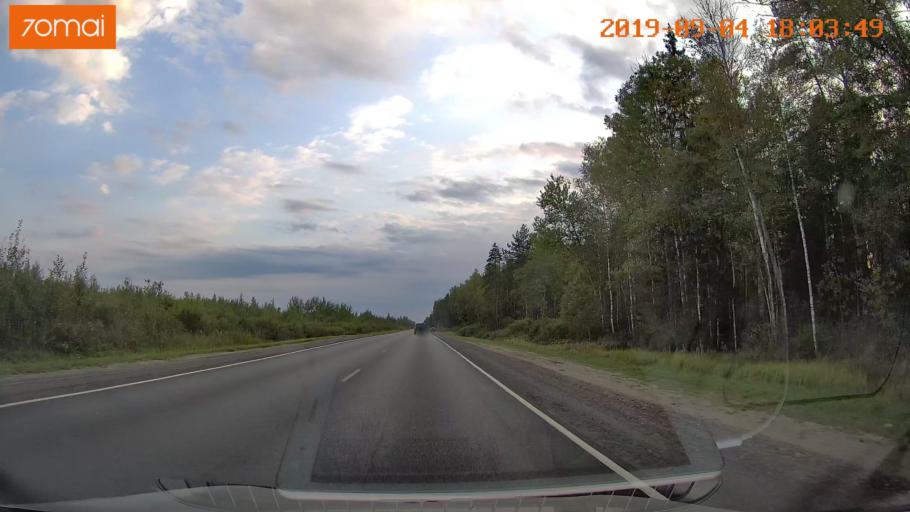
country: RU
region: Moskovskaya
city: Il'inskiy Pogost
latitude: 55.4593
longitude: 38.8473
